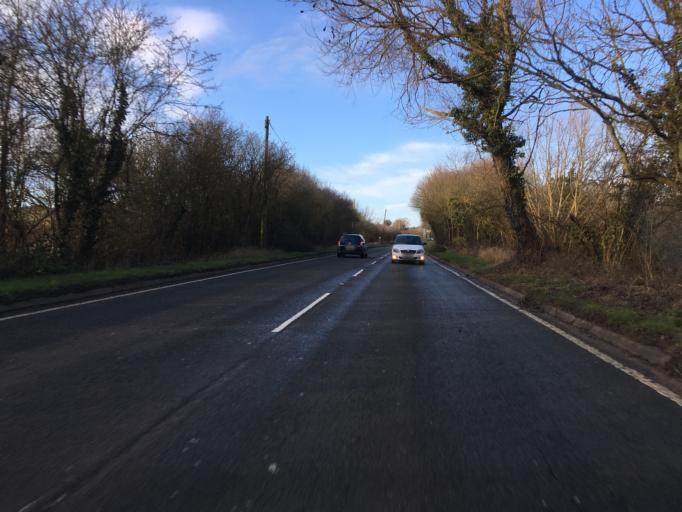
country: GB
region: England
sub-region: Warwickshire
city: Stratford-upon-Avon
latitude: 52.2137
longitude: -1.7267
